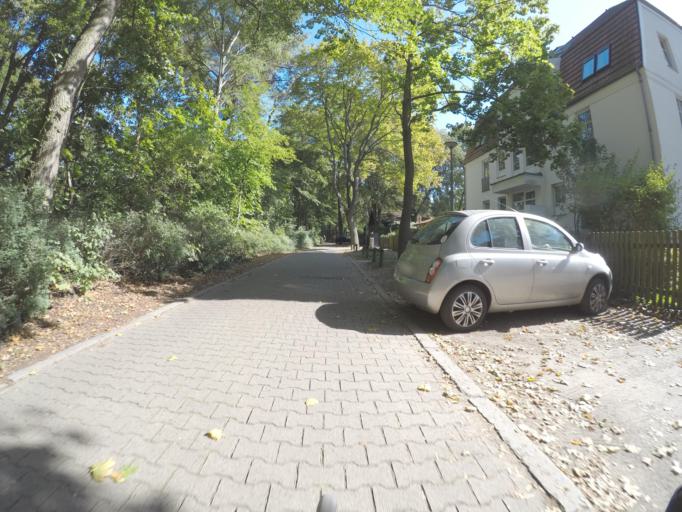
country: DE
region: Berlin
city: Konradshohe
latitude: 52.5792
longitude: 13.2202
